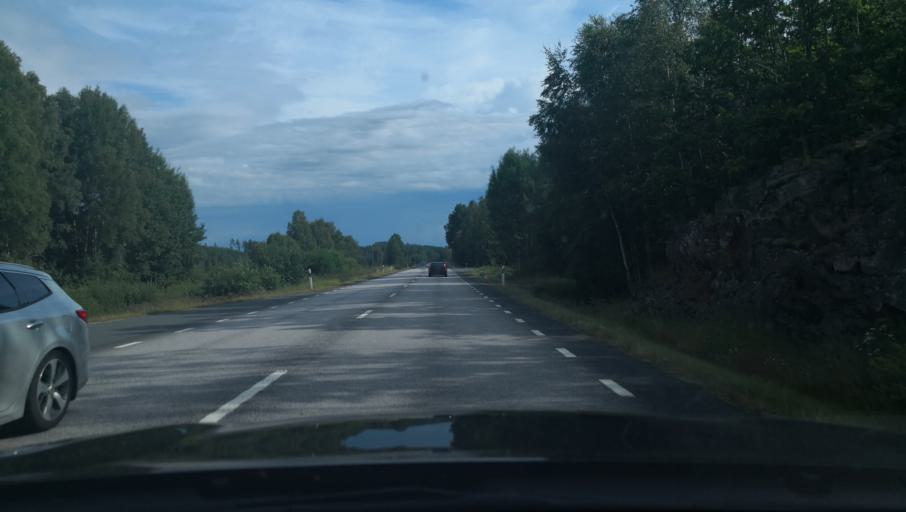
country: SE
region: Kalmar
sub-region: Hultsfreds Kommun
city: Hultsfred
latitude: 57.5730
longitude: 15.8454
